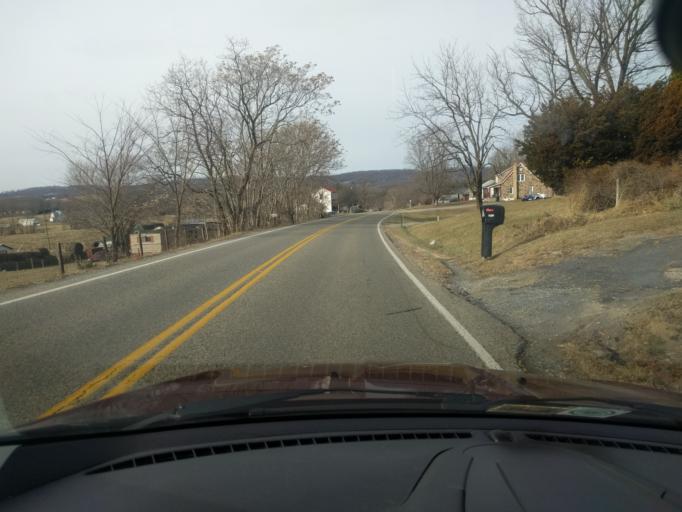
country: US
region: Virginia
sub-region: Augusta County
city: Stuarts Draft
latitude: 38.0420
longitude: -79.0836
